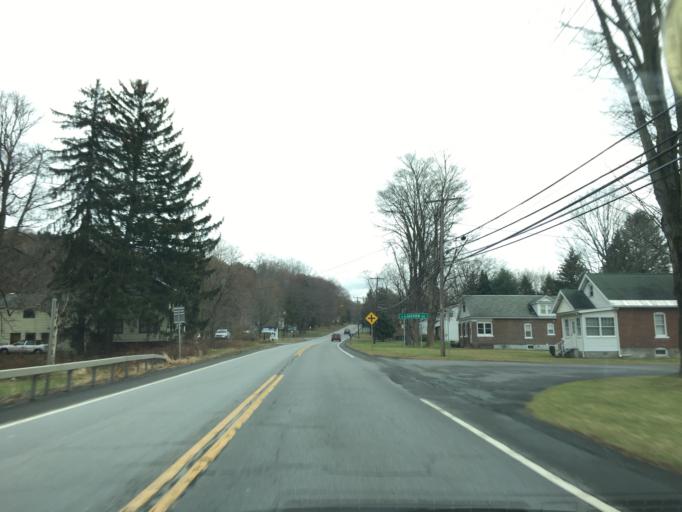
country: US
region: New York
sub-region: Rensselaer County
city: Wynantskill
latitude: 42.6926
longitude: -73.6304
